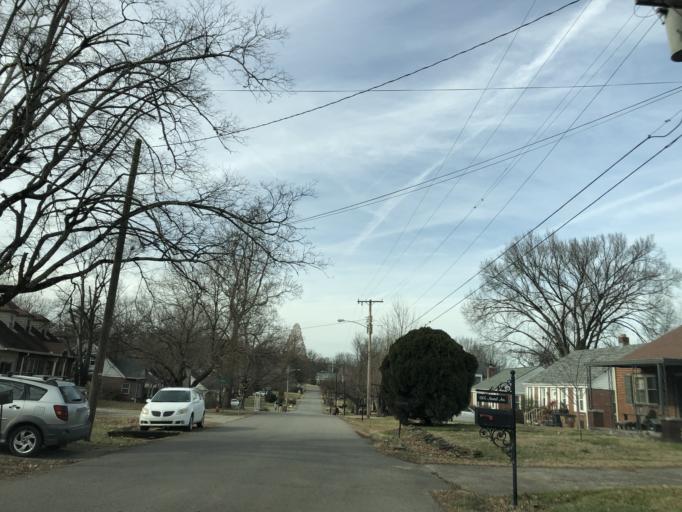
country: US
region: Tennessee
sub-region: Davidson County
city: Nashville
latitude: 36.2164
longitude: -86.7255
